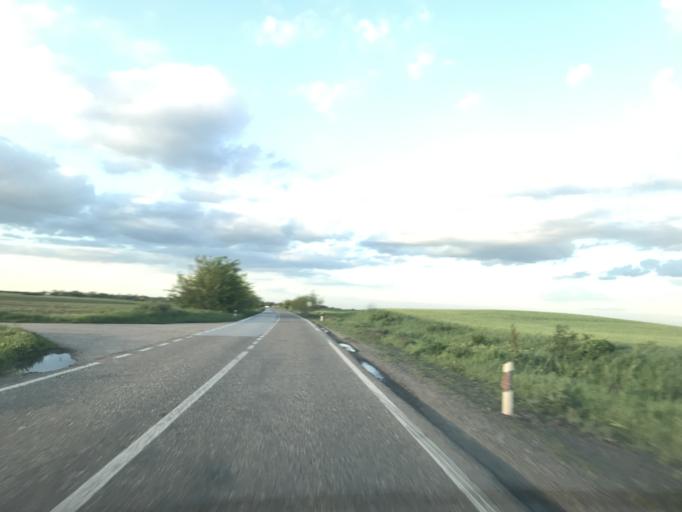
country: RS
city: Cestereg
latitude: 45.5489
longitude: 20.5141
